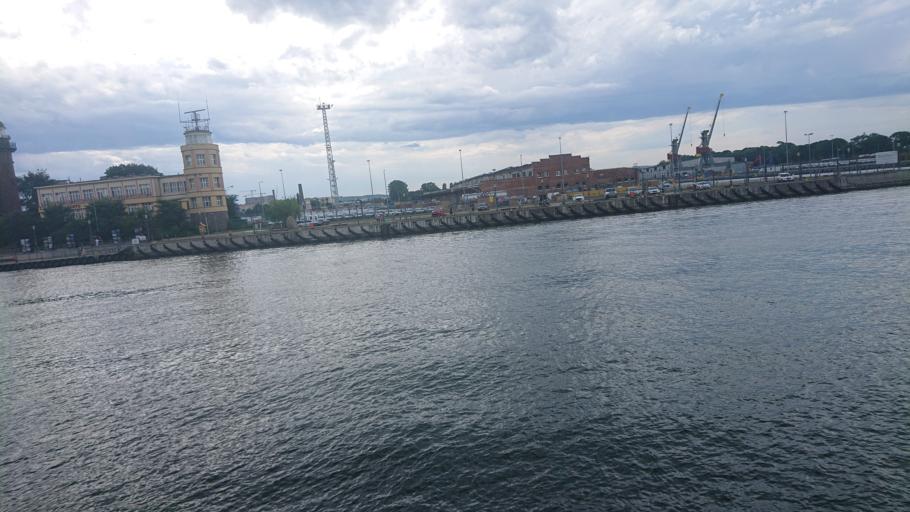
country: PL
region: Pomeranian Voivodeship
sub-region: Gdansk
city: Gdansk
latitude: 54.4078
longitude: 18.6625
